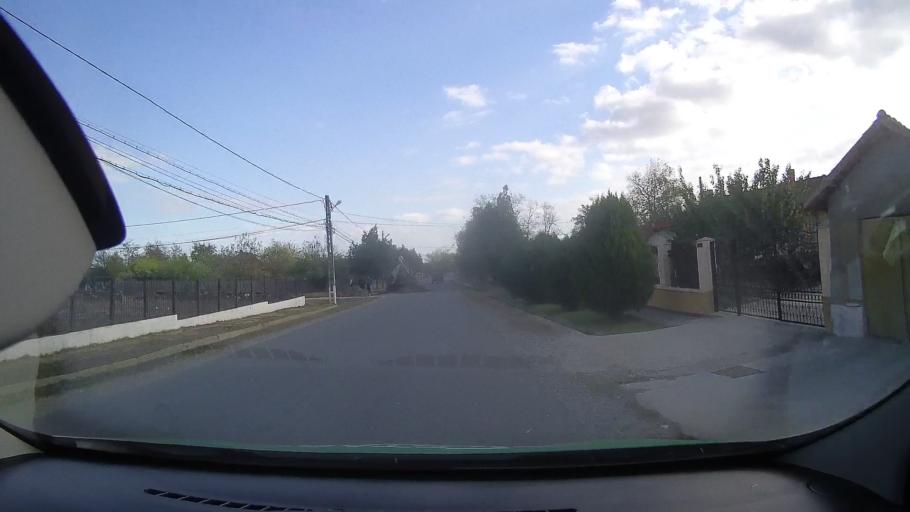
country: RO
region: Constanta
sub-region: Comuna Sacele
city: Sacele
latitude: 44.4879
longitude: 28.6423
